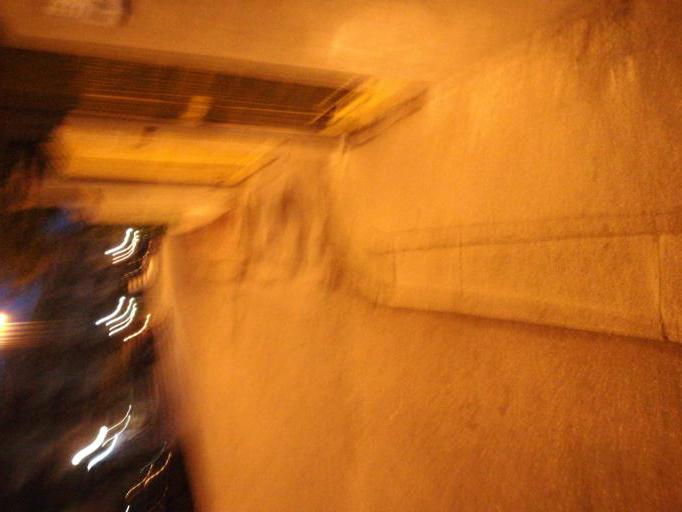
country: IT
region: Apulia
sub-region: Provincia di Bari
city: San Paolo
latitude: 41.1251
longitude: 16.7838
